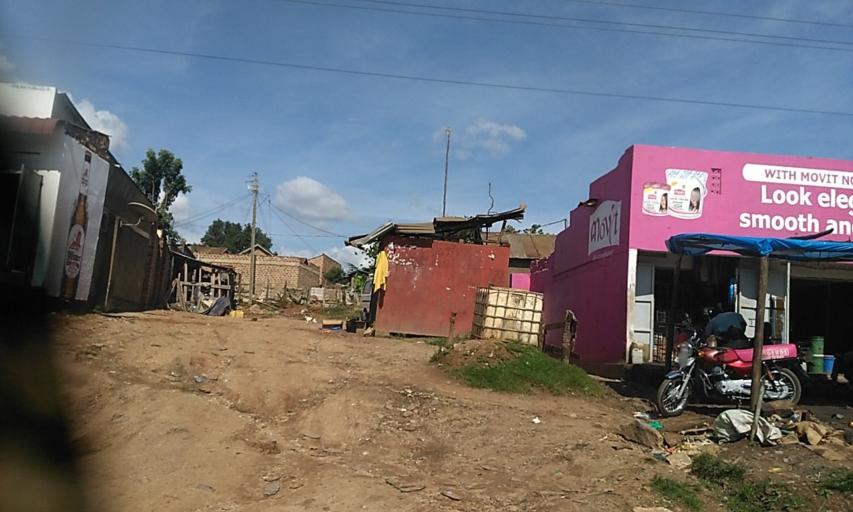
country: UG
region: Central Region
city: Kampala Central Division
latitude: 0.3988
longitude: 32.5465
